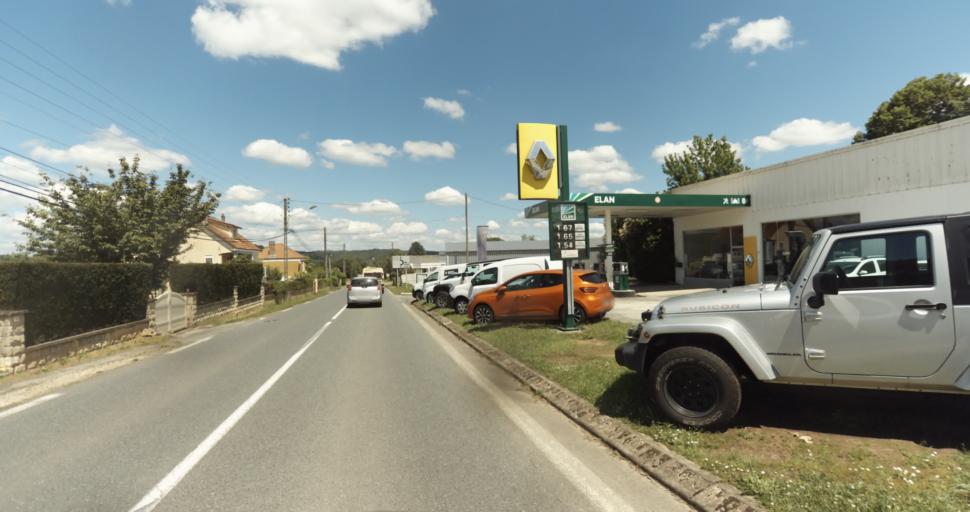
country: FR
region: Aquitaine
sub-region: Departement de la Dordogne
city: Le Bugue
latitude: 44.8468
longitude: 0.8989
